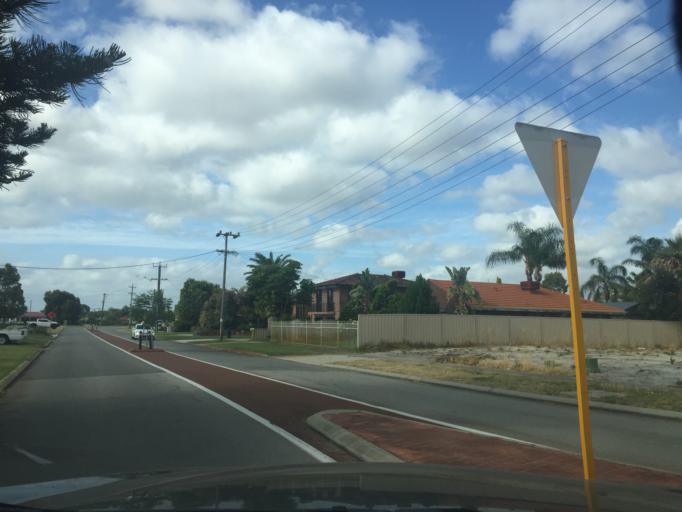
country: AU
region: Western Australia
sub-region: Canning
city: Canning Vale
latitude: -32.0453
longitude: 115.9099
